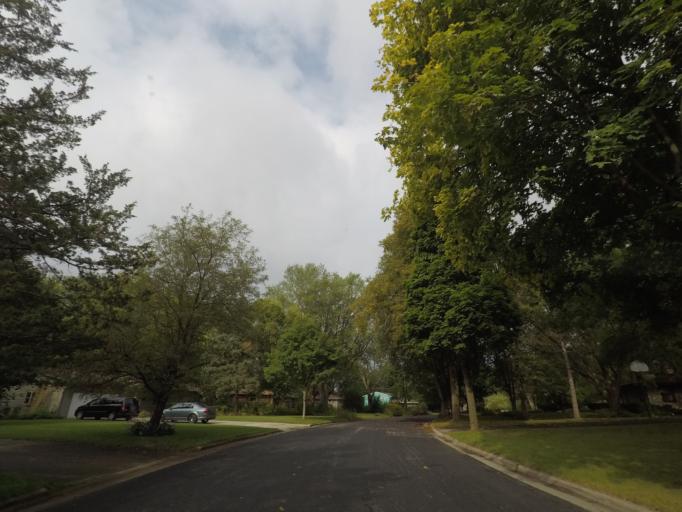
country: US
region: Wisconsin
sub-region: Dane County
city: Shorewood Hills
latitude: 43.0369
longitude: -89.4809
